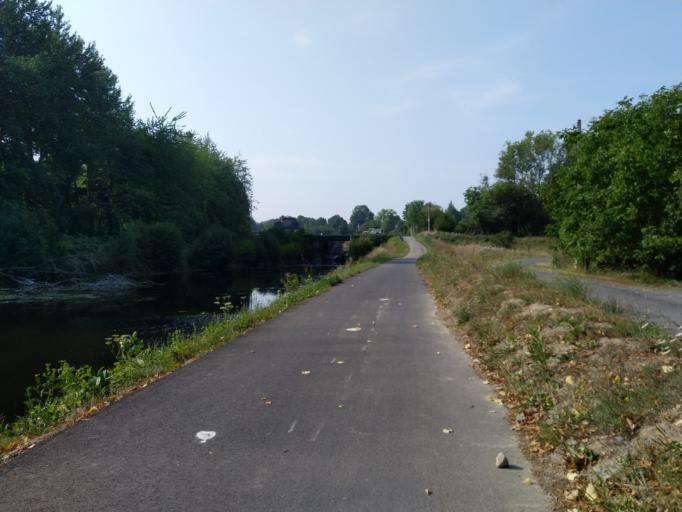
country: BE
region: Wallonia
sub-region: Province du Hainaut
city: Seneffe
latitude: 50.5788
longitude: 4.2530
